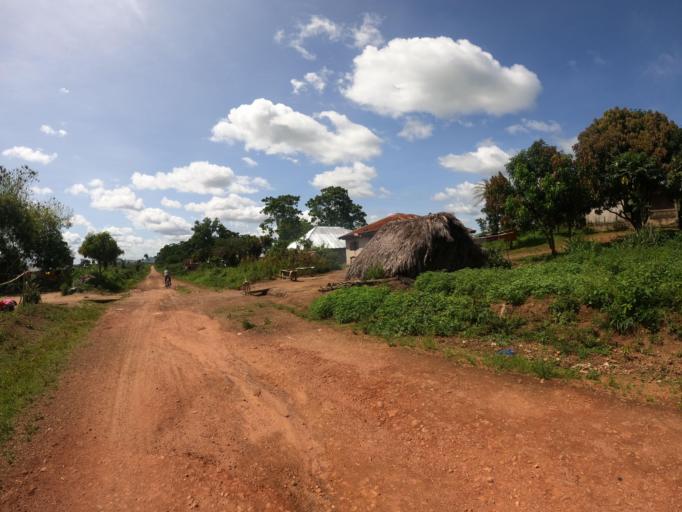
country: SL
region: Northern Province
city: Masingbi
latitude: 8.8317
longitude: -11.9928
